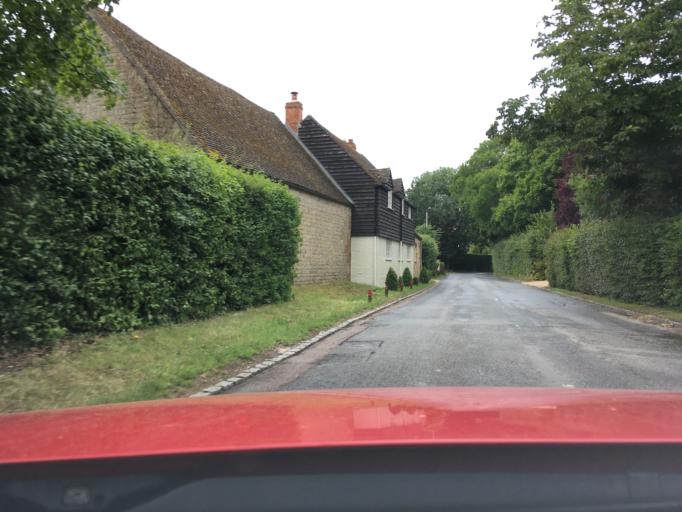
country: GB
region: England
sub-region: Warwickshire
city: Shipston on Stour
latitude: 52.1005
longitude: -1.6427
